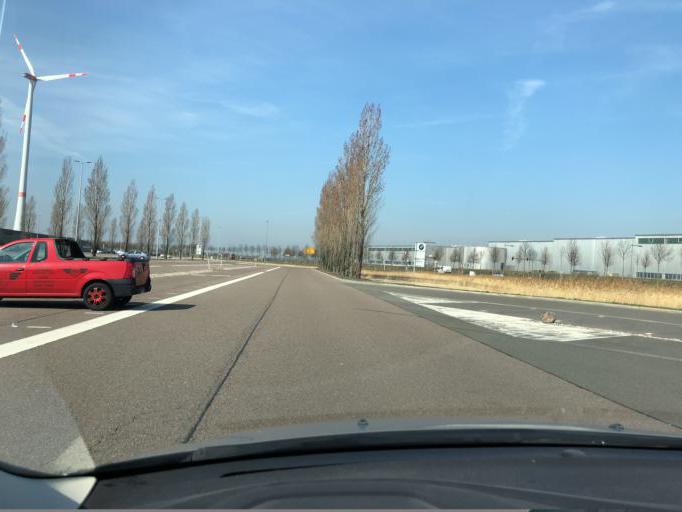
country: DE
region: Saxony
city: Taucha
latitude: 51.4111
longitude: 12.4423
